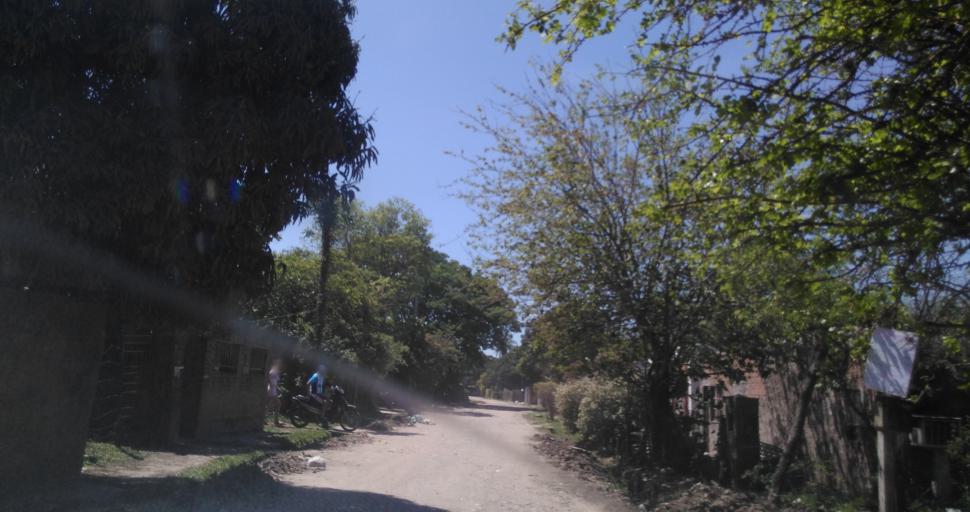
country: AR
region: Chaco
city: Resistencia
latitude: -27.4253
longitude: -58.9810
